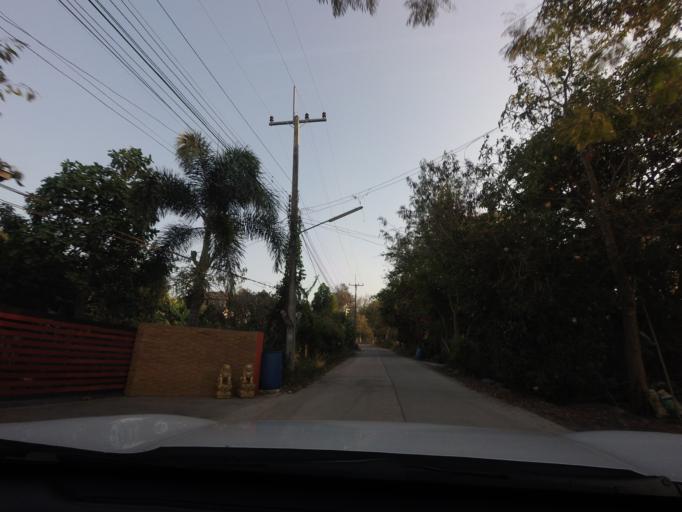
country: TH
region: Nakhon Ratchasima
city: Pak Chong
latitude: 14.6497
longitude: 101.3881
